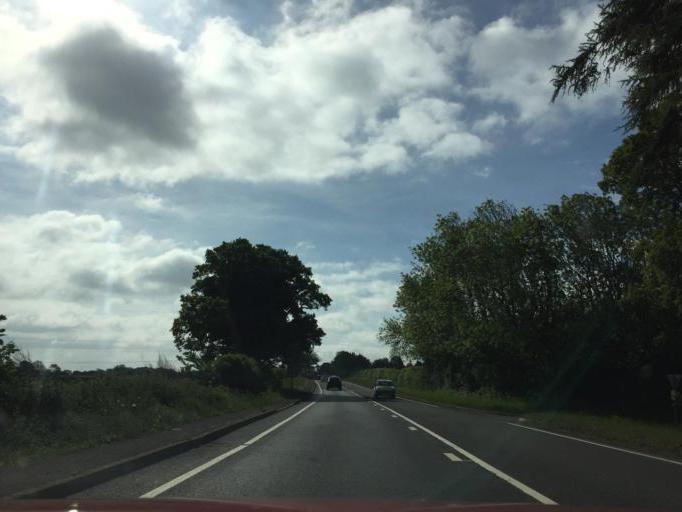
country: GB
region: England
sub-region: Northamptonshire
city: Towcester
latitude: 52.1081
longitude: -0.9455
